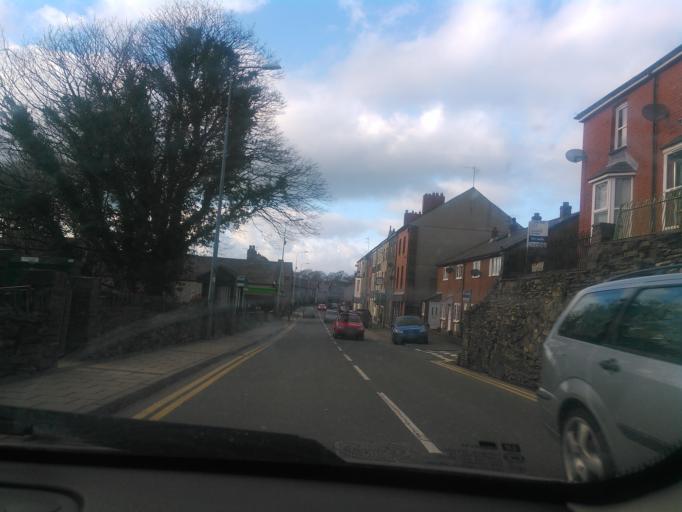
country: GB
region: Wales
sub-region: Gwynedd
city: Bethesda
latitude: 53.1811
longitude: -4.0651
